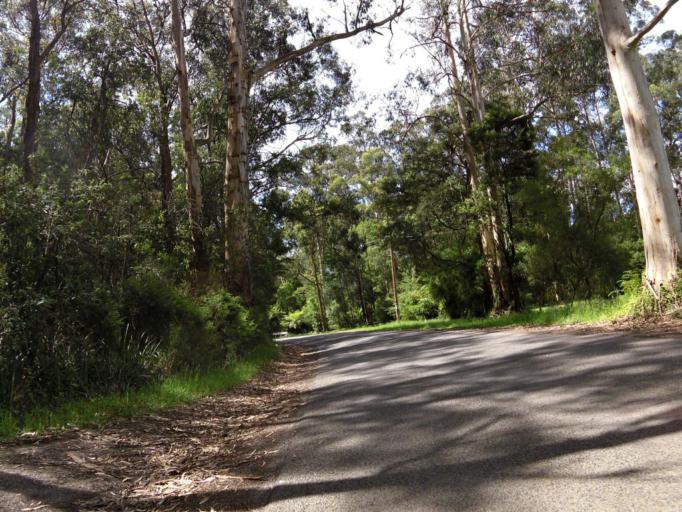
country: AU
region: Victoria
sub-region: Yarra Ranges
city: Millgrove
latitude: -37.7513
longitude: 145.7302
